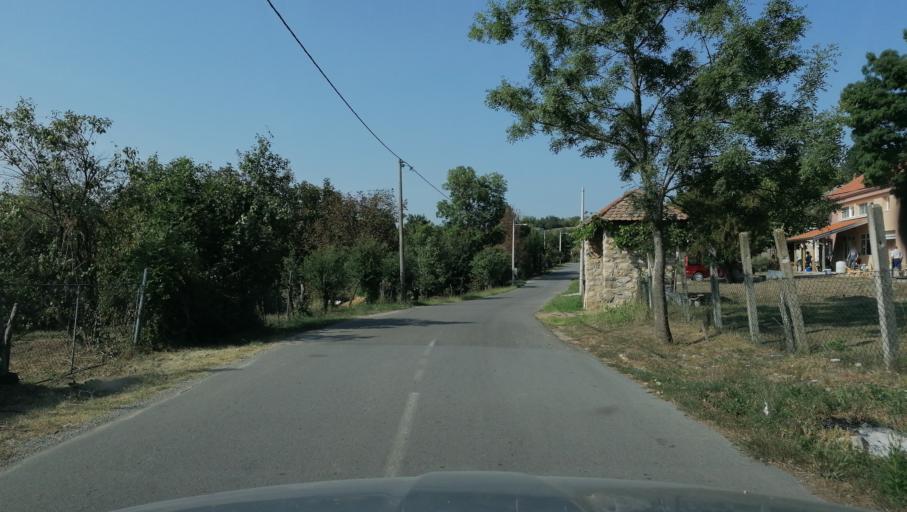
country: RS
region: Central Serbia
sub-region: Belgrade
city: Sopot
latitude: 44.5881
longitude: 20.6104
